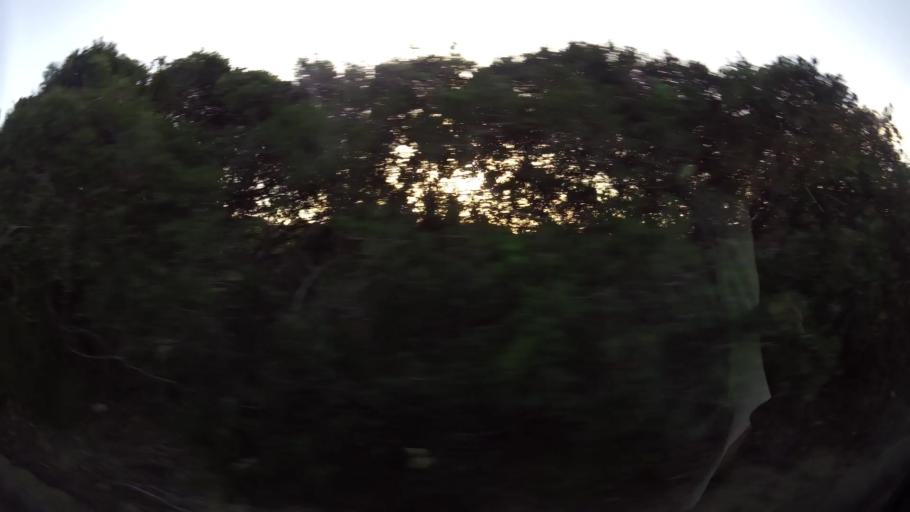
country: ZA
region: Western Cape
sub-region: Eden District Municipality
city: George
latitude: -34.0029
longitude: 22.6468
